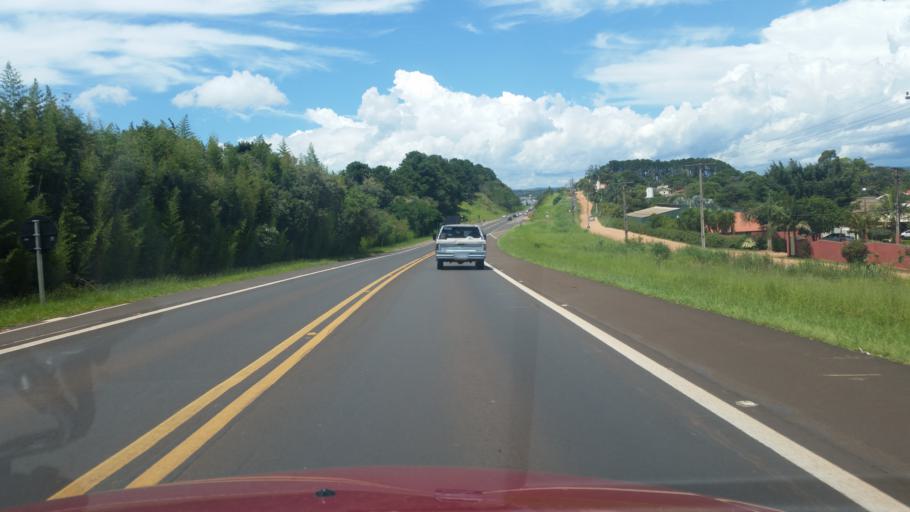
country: BR
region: Sao Paulo
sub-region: Itai
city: Itai
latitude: -23.2796
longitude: -49.0254
